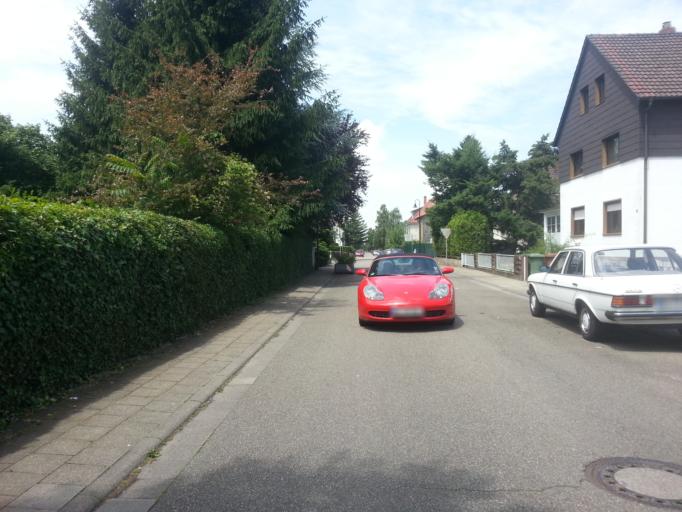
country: DE
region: Baden-Wuerttemberg
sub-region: Karlsruhe Region
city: Edingen-Neckarhausen
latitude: 49.4461
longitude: 8.5833
